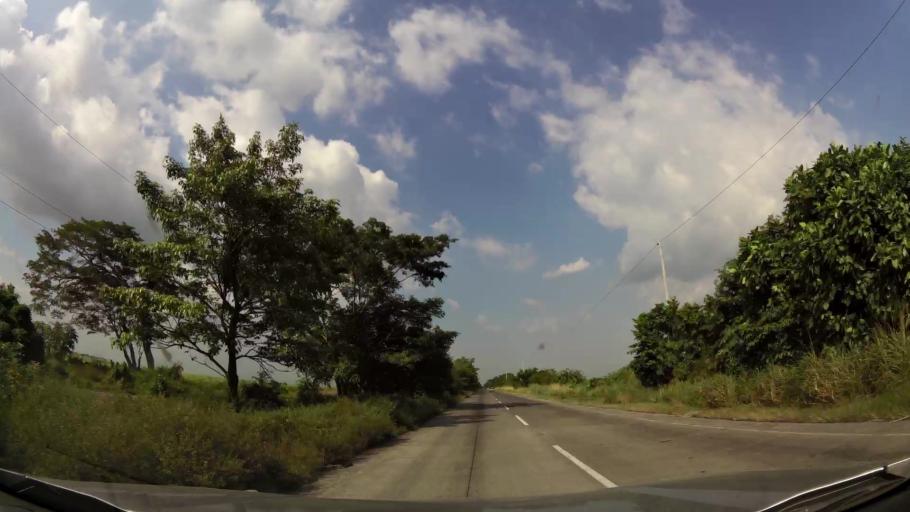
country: GT
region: Escuintla
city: Puerto San Jose
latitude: 14.0312
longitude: -90.7808
